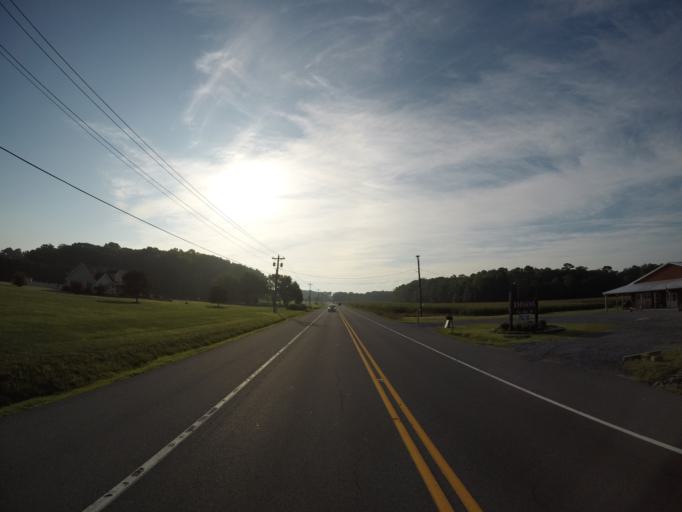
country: US
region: Delaware
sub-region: Sussex County
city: Ocean View
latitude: 38.4754
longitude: -75.1330
